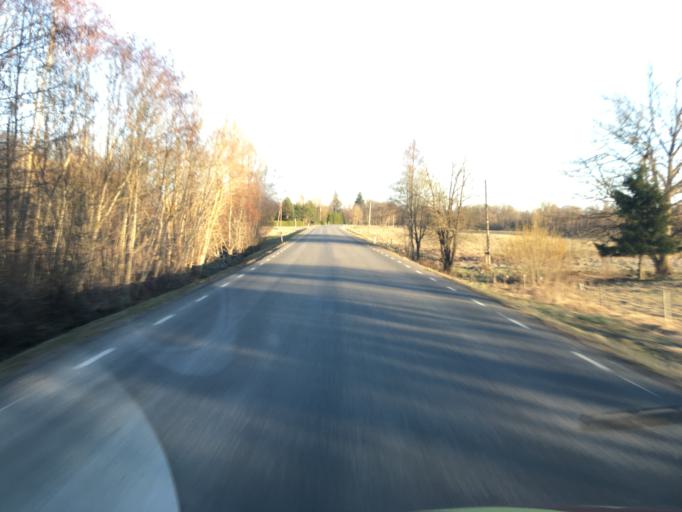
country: EE
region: Raplamaa
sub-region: Kehtna vald
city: Kehtna
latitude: 59.0279
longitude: 24.9241
